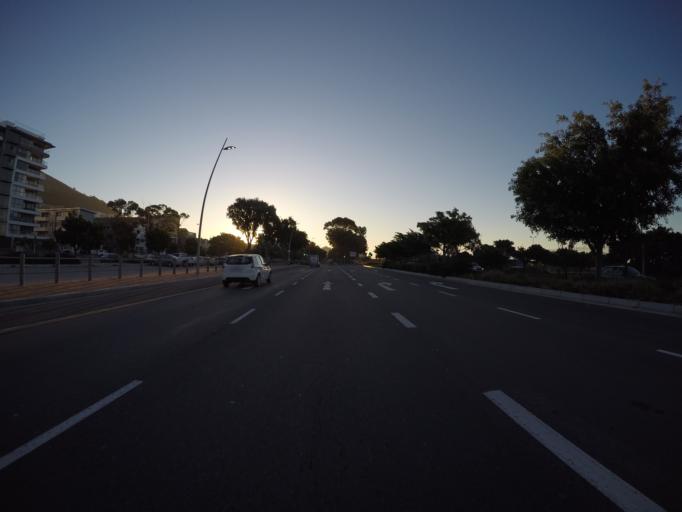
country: ZA
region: Western Cape
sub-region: City of Cape Town
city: Cape Town
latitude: -33.9071
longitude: 18.4078
